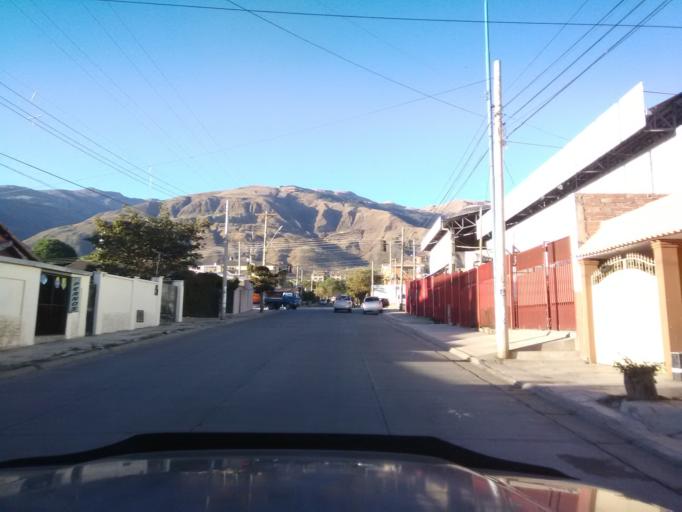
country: BO
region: Cochabamba
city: Cochabamba
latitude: -17.3549
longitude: -66.1809
